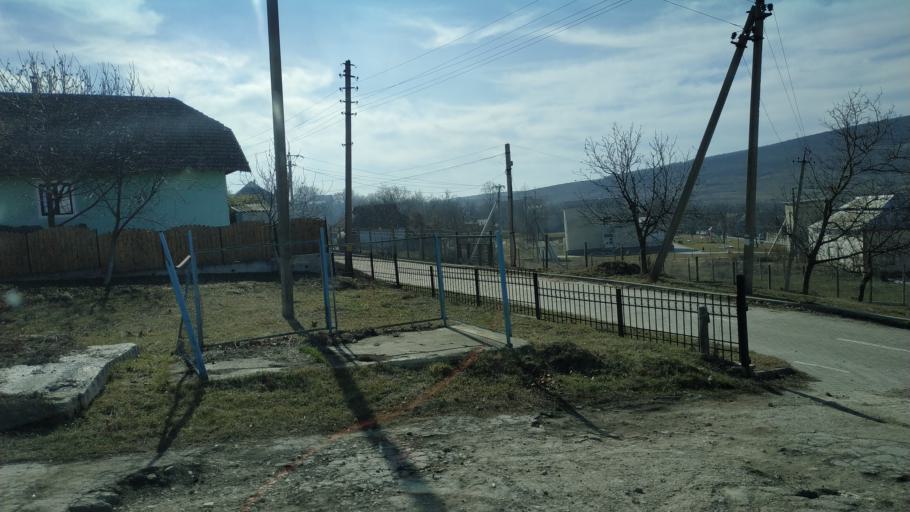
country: MD
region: Nisporeni
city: Nisporeni
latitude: 47.0781
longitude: 28.2624
